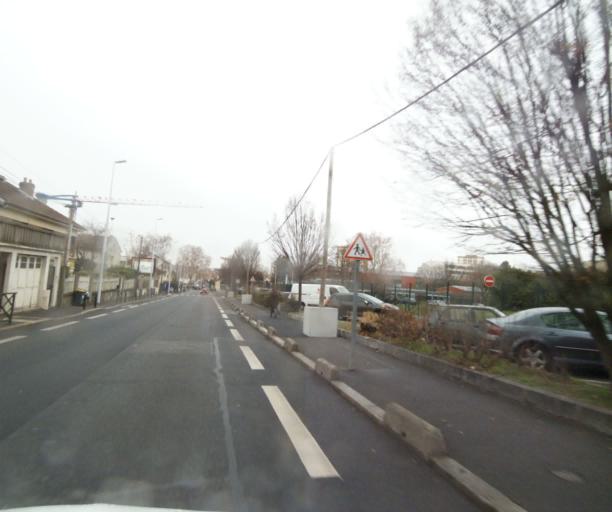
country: FR
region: Ile-de-France
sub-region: Departement des Hauts-de-Seine
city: Nanterre
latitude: 48.8878
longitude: 2.2065
